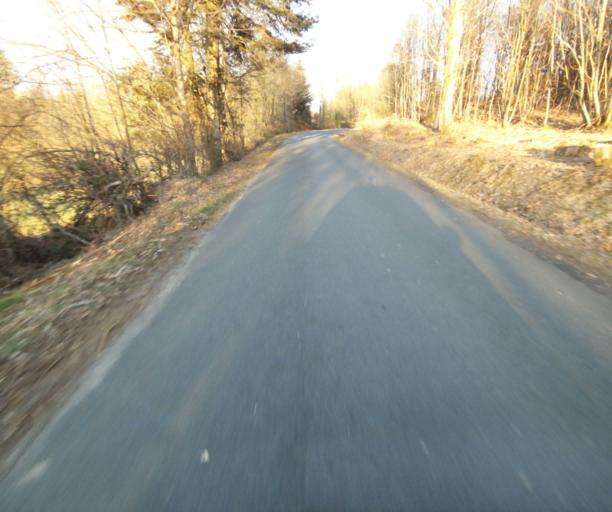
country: FR
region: Limousin
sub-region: Departement de la Correze
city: Saint-Clement
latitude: 45.3243
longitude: 1.6771
